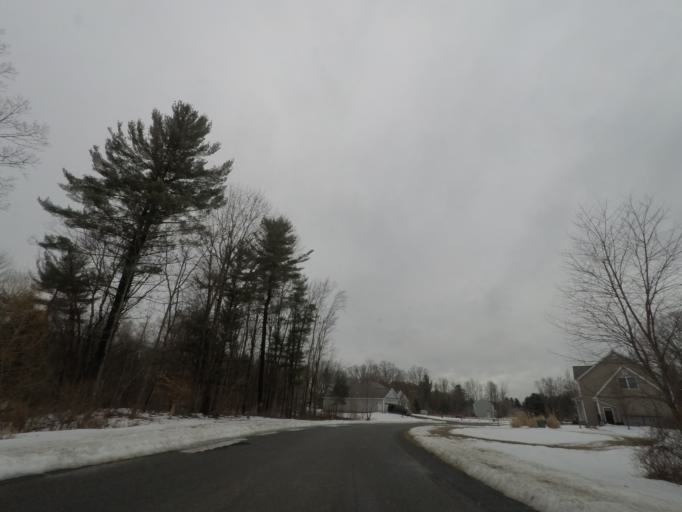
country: US
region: New York
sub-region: Schenectady County
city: Rotterdam
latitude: 42.7613
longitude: -73.9702
